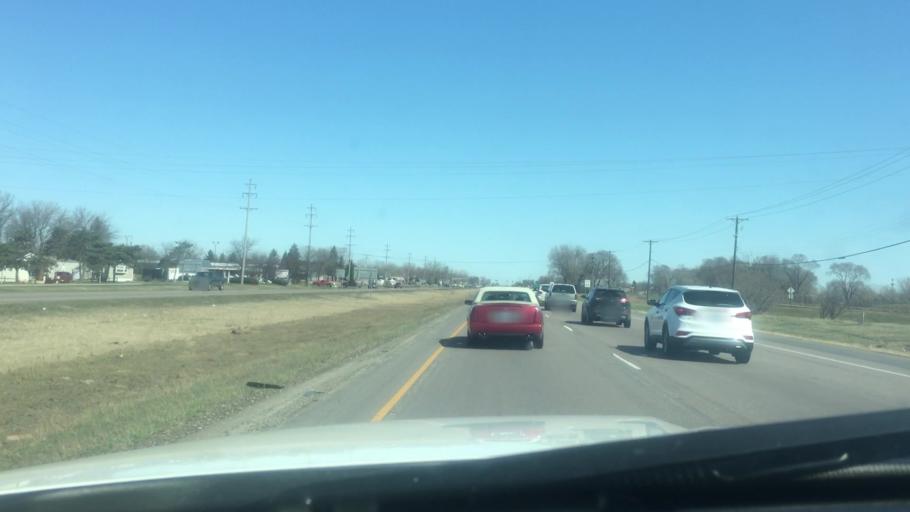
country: US
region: Minnesota
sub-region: Anoka County
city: Blaine
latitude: 45.1441
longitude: -93.2351
